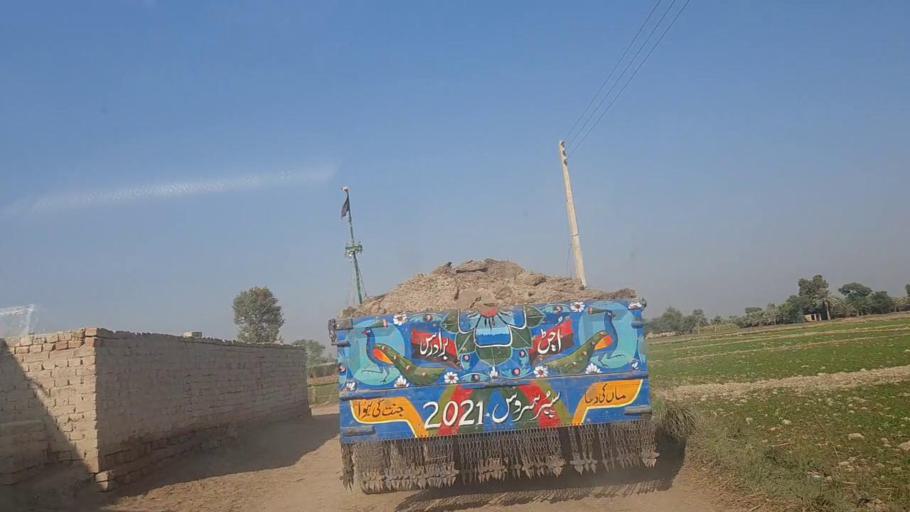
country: PK
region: Sindh
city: Gambat
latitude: 27.3663
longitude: 68.4759
